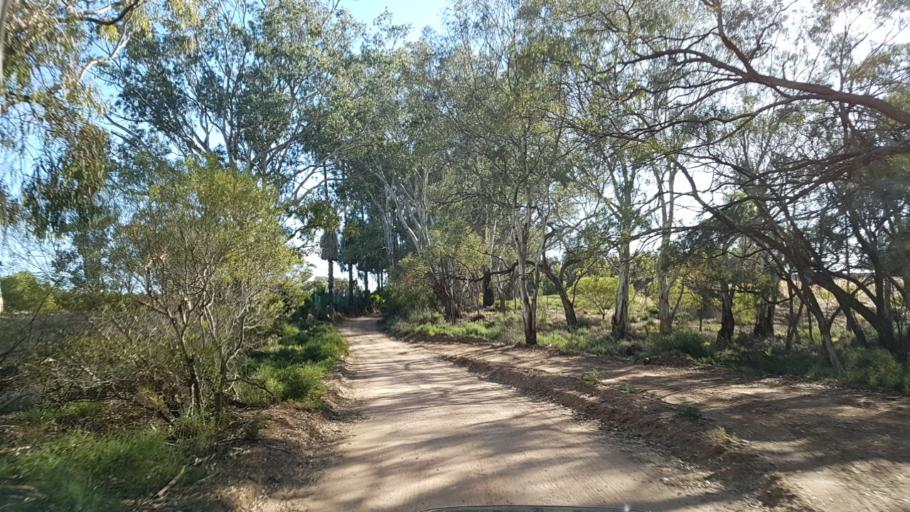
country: AU
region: South Australia
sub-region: Loxton Waikerie
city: Waikerie
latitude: -34.1631
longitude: 140.0332
